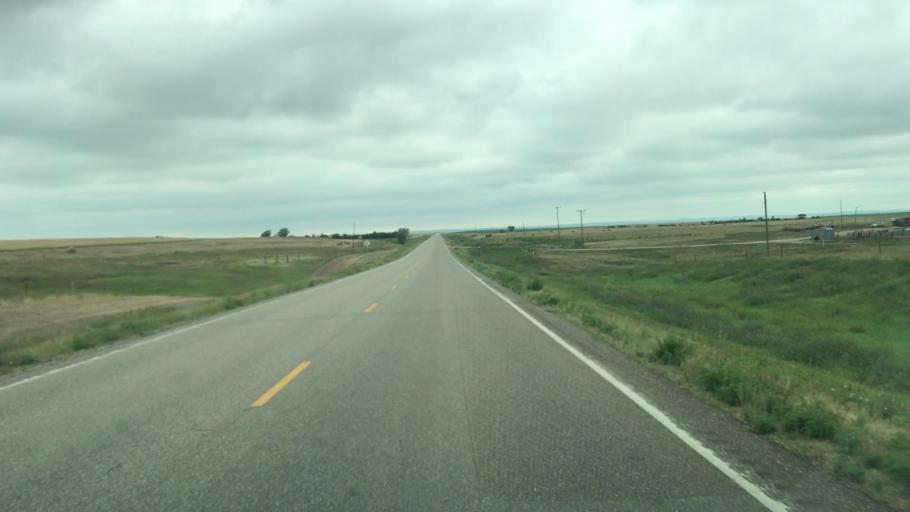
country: US
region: South Dakota
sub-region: Jackson County
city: Kadoka
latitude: 43.8269
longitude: -101.5224
